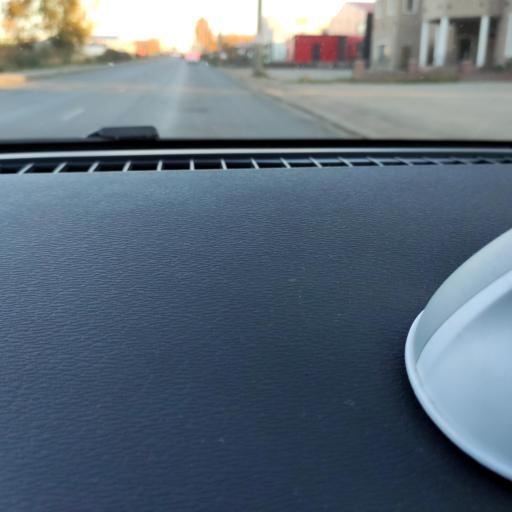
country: RU
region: Samara
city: Petra-Dubrava
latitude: 53.2539
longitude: 50.2666
